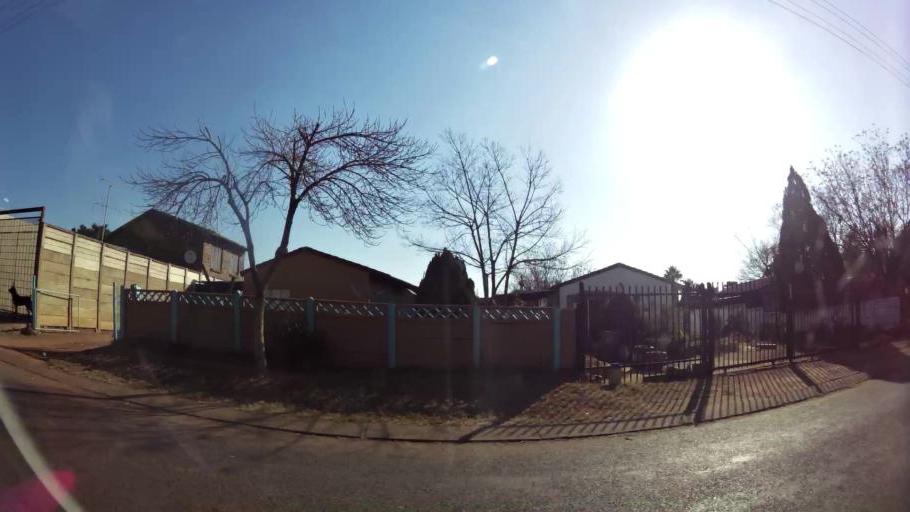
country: ZA
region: Gauteng
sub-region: City of Tshwane Metropolitan Municipality
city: Pretoria
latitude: -25.7112
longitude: 28.1395
